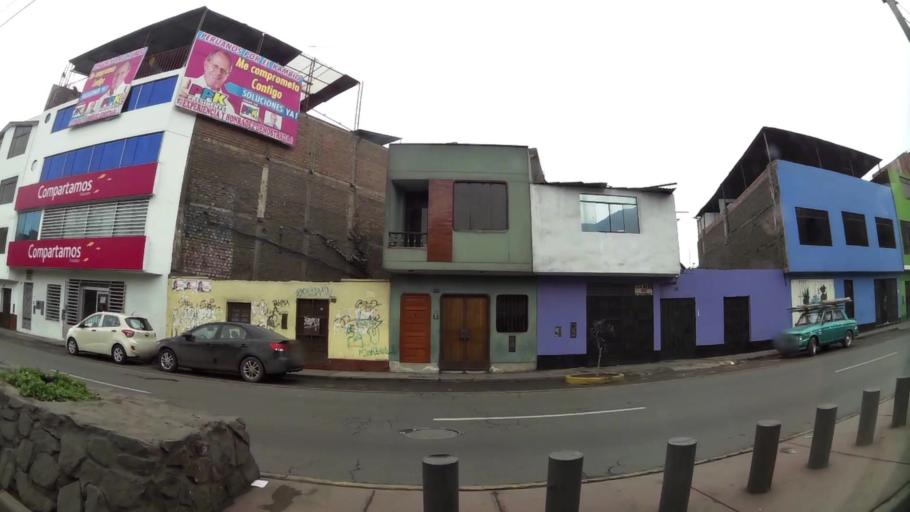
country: PE
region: Lima
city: Lima
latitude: -12.0471
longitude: -77.0000
